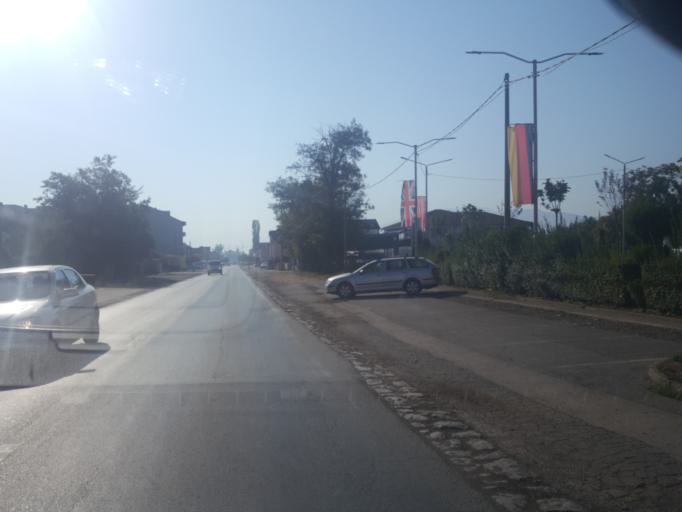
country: XK
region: Gjakova
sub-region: Komuna e Gjakoves
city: Gjakove
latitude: 42.4054
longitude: 20.4097
